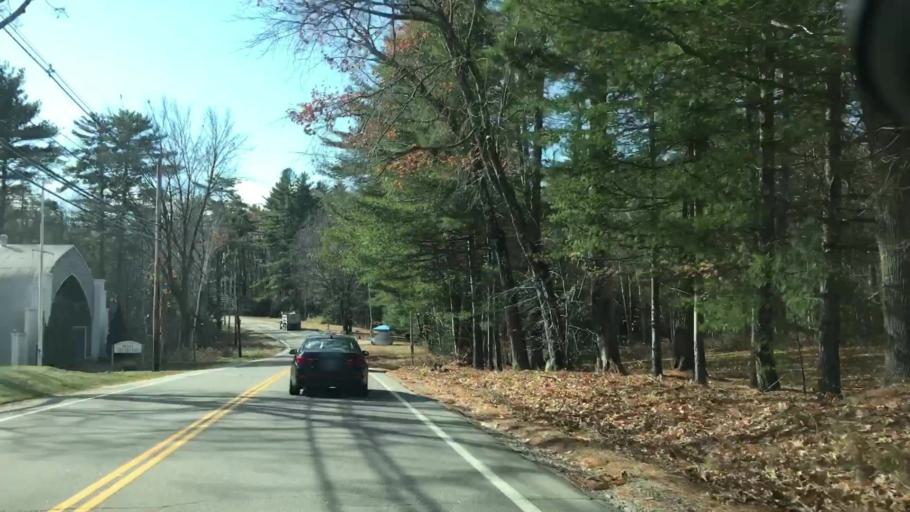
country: US
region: New Hampshire
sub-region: Carroll County
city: Wolfeboro
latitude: 43.6061
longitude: -71.1881
